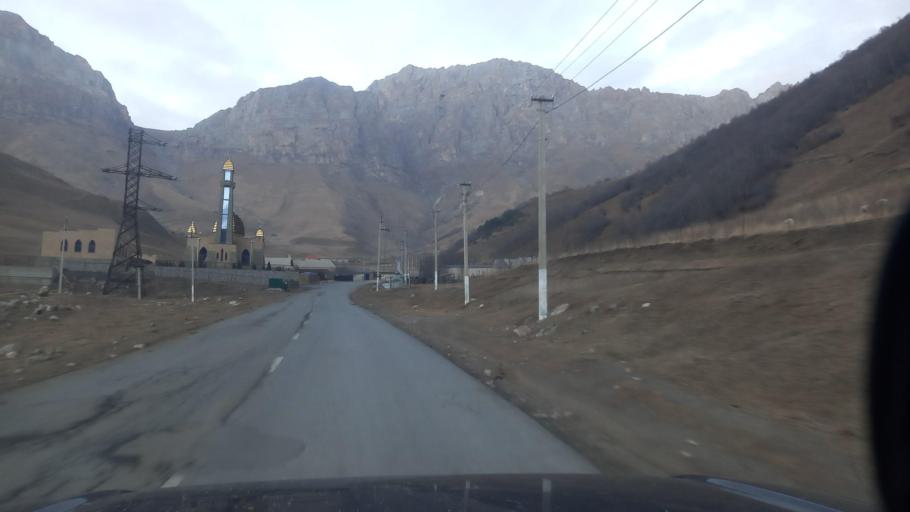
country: RU
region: Ingushetiya
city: Dzhayrakh
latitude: 42.8142
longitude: 44.8130
